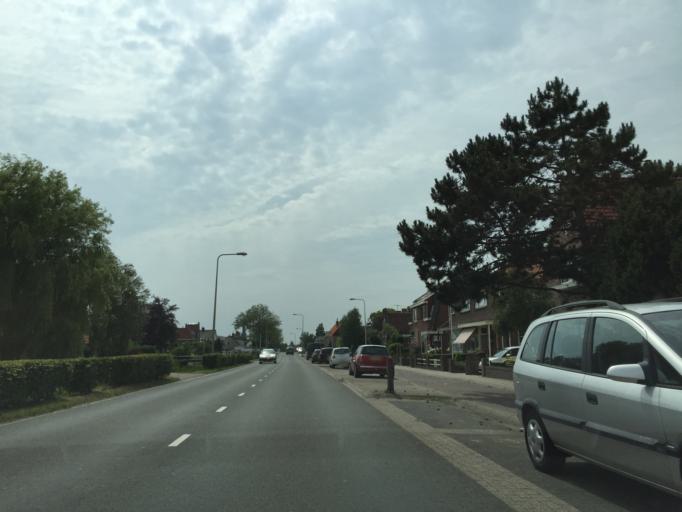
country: NL
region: South Holland
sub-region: Gemeente Westland
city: Kwintsheul
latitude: 52.0198
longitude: 4.2633
